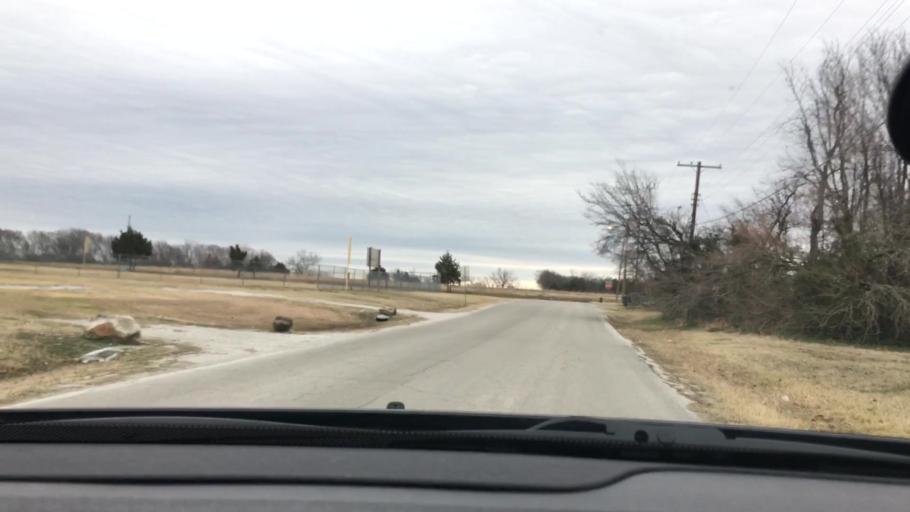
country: US
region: Oklahoma
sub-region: Carter County
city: Ardmore
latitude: 34.1692
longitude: -97.1095
